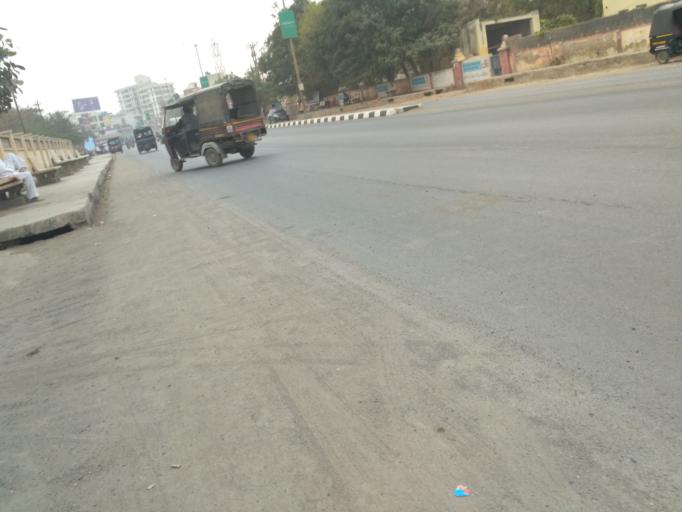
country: IN
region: Gujarat
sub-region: Porbandar
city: Porbandar
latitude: 21.6397
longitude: 69.6250
